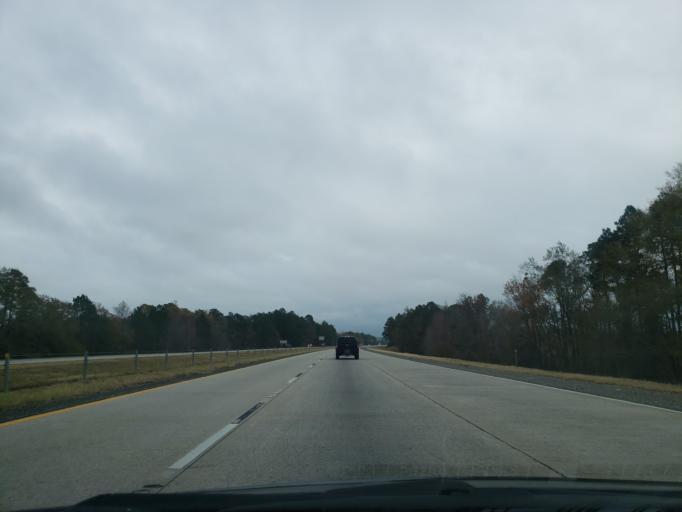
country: US
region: Georgia
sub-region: Treutlen County
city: Soperton
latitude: 32.4341
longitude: -82.6012
